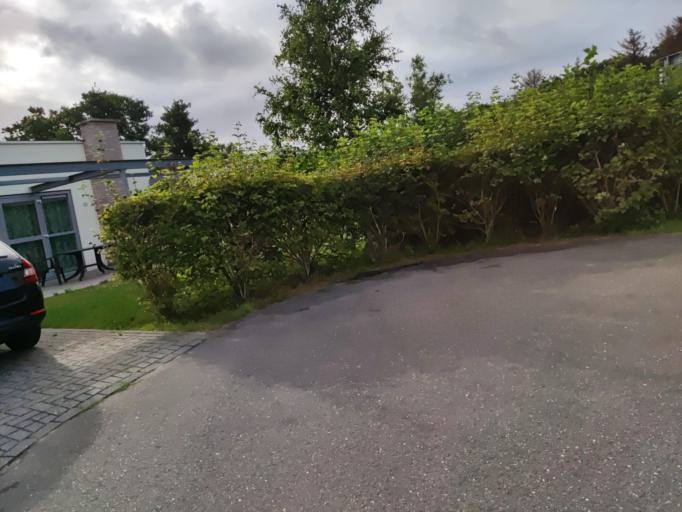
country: NL
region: North Holland
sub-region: Gemeente Texel
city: Den Burg
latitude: 53.0903
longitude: 4.7677
